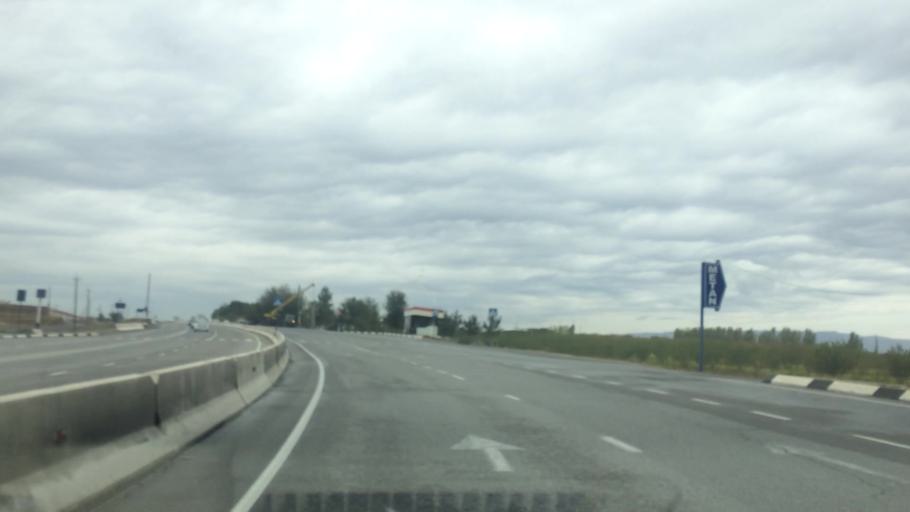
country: UZ
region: Jizzax
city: Jizzax
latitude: 39.9771
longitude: 67.5627
